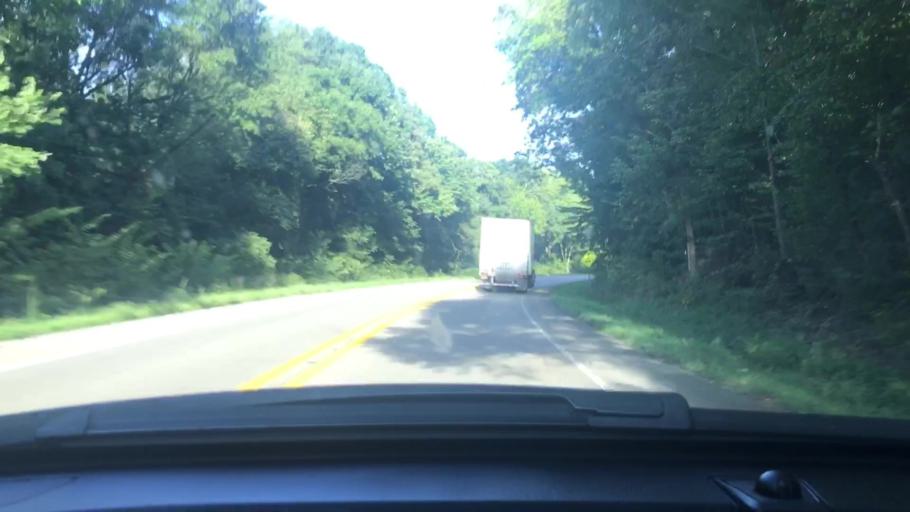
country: US
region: Arkansas
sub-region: Randolph County
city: Pocahontas
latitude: 36.2128
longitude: -91.2073
